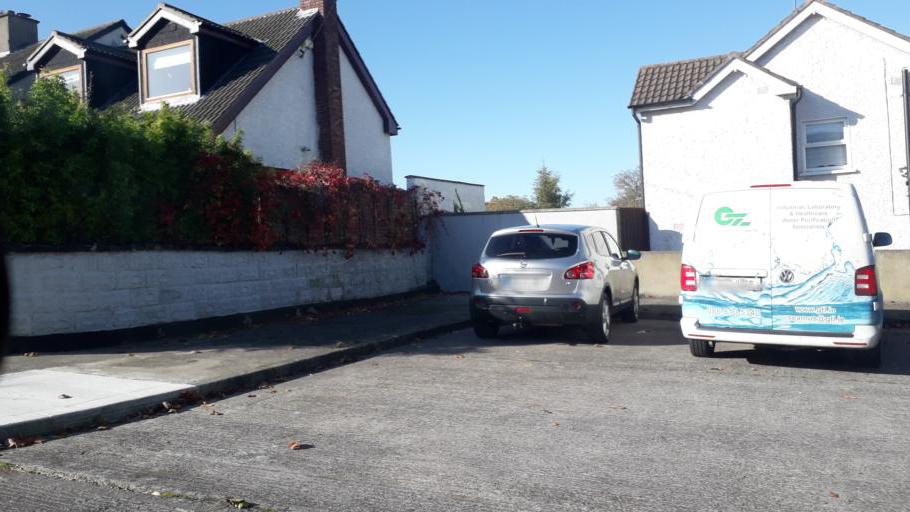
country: IE
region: Leinster
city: Raheny
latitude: 53.3810
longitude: -6.1841
